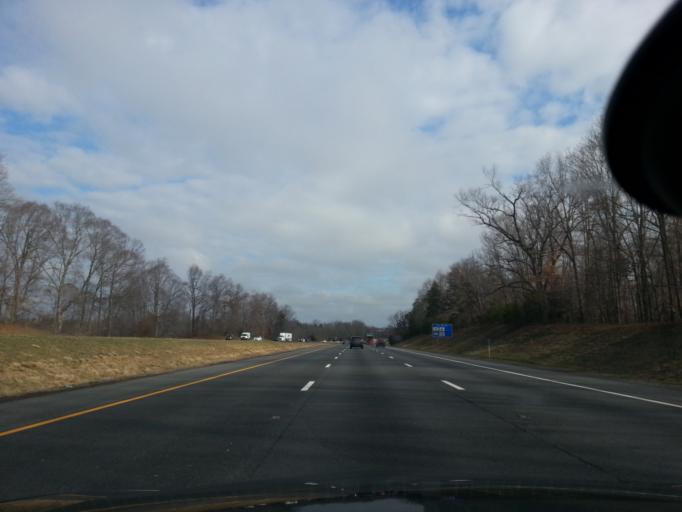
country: US
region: Virginia
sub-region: Spotsylvania County
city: Spotsylvania Courthouse
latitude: 38.1103
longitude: -77.5178
